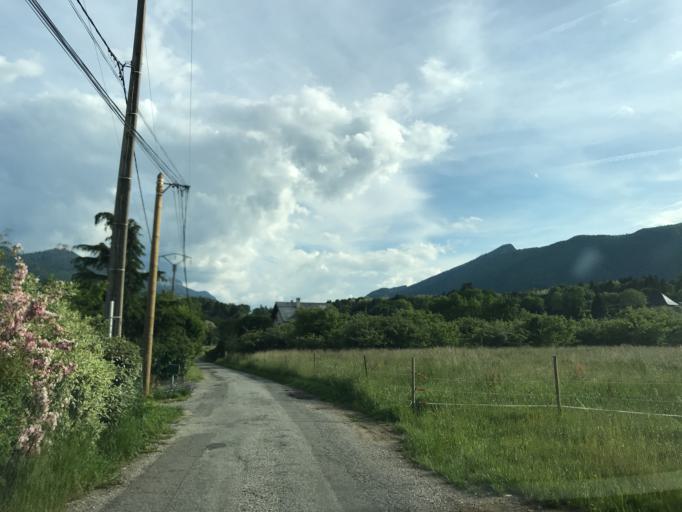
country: FR
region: Rhone-Alpes
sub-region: Departement de la Savoie
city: Vimines
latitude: 45.5599
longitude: 5.8644
